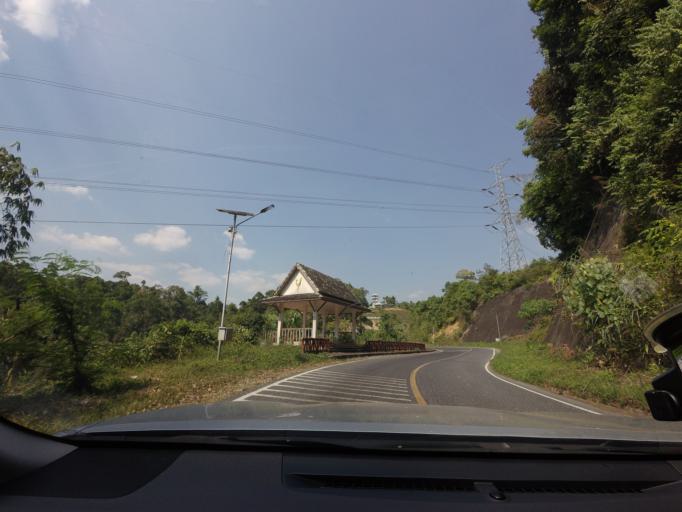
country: TH
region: Phangnga
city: Thap Put
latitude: 8.5342
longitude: 98.5581
